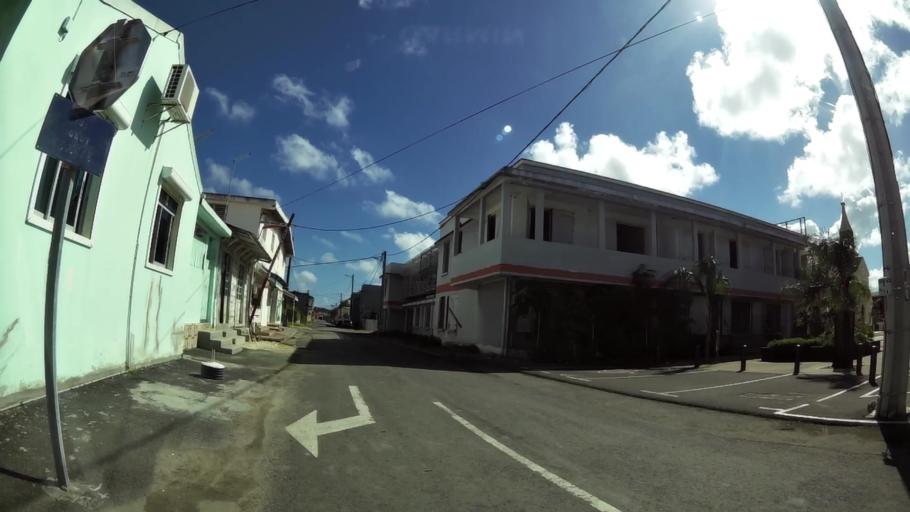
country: GP
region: Guadeloupe
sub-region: Guadeloupe
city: Port-Louis
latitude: 16.4185
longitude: -61.5334
